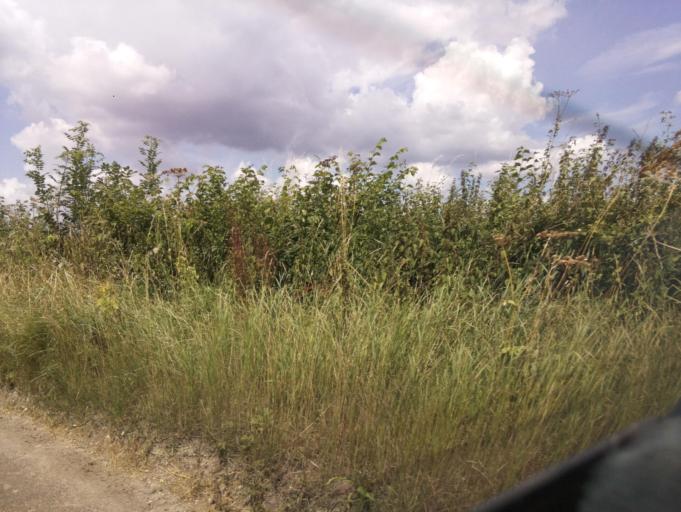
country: GB
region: England
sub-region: Borough of Swindon
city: Bishopstone
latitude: 51.5717
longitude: -1.6332
